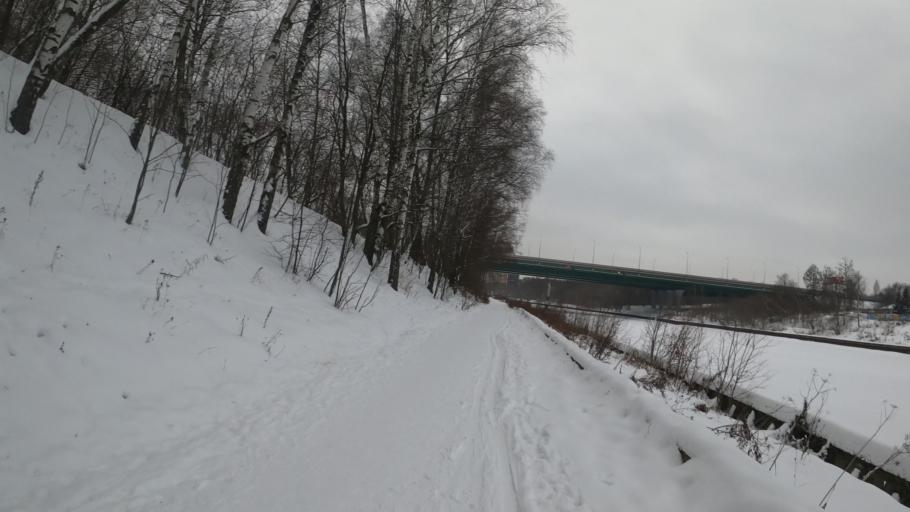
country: RU
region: Moskovskaya
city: Levoberezhnaya
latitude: 55.9099
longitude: 37.4771
